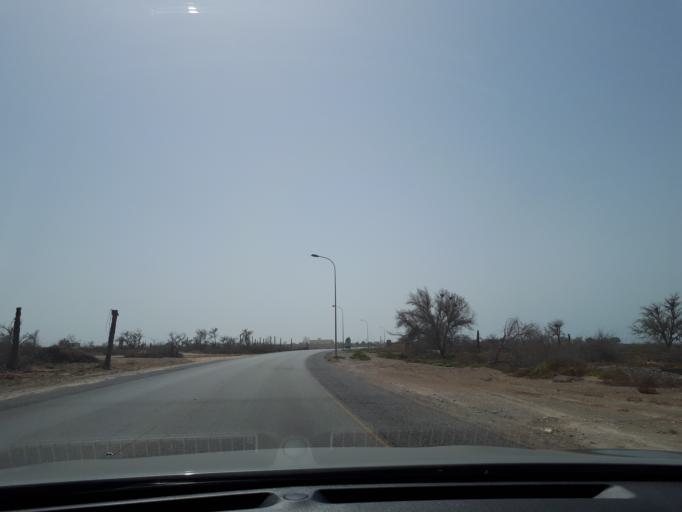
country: OM
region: Al Batinah
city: Barka'
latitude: 23.7016
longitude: 57.9472
